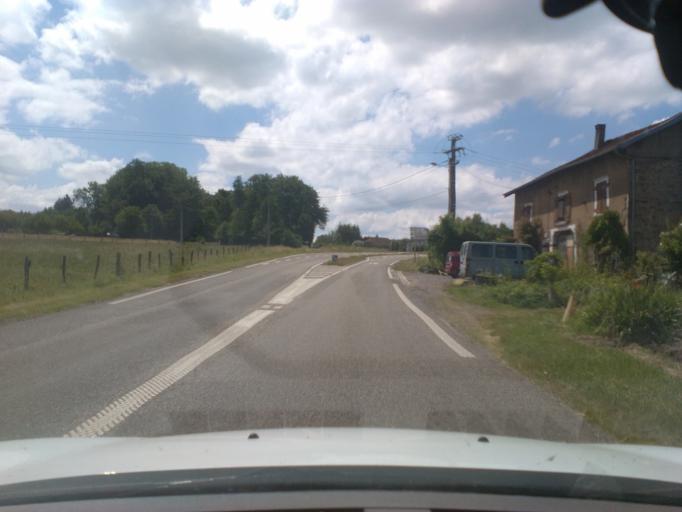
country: FR
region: Lorraine
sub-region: Departement des Vosges
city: Aydoilles
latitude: 48.2178
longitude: 6.5811
